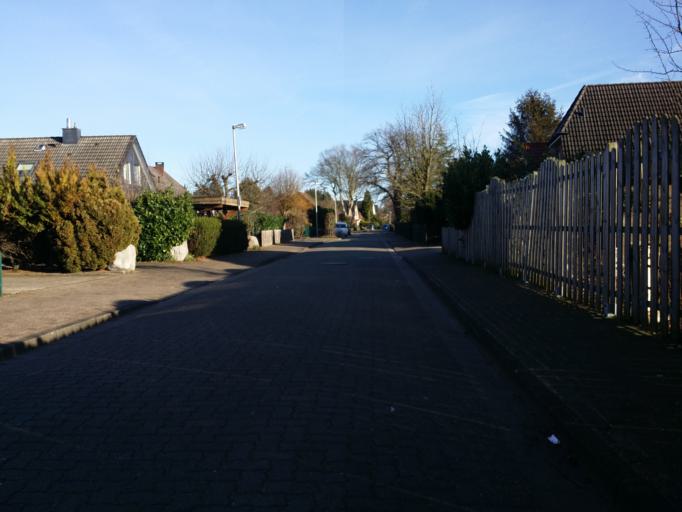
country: DE
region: Lower Saxony
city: Delmenhorst
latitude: 53.0540
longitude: 8.6669
